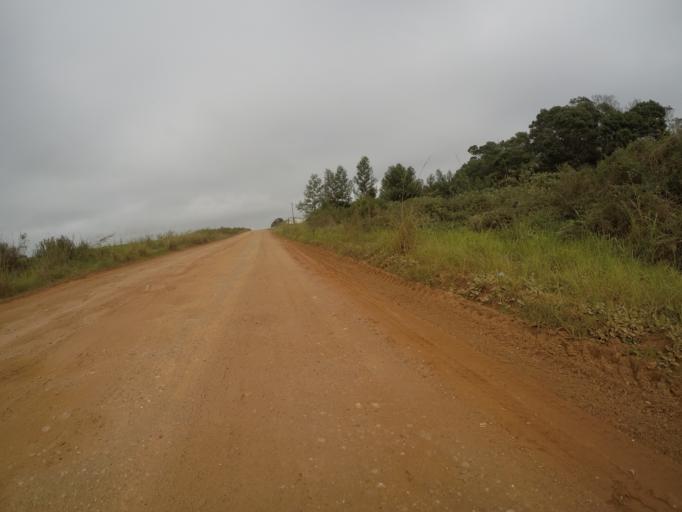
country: ZA
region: Eastern Cape
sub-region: Cacadu District Municipality
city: Kareedouw
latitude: -34.0152
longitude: 24.2381
